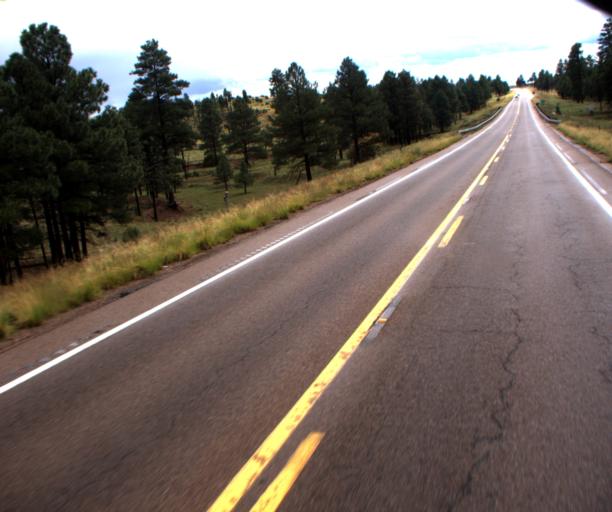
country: US
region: Arizona
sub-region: Navajo County
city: Heber-Overgaard
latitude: 34.3728
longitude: -110.4590
